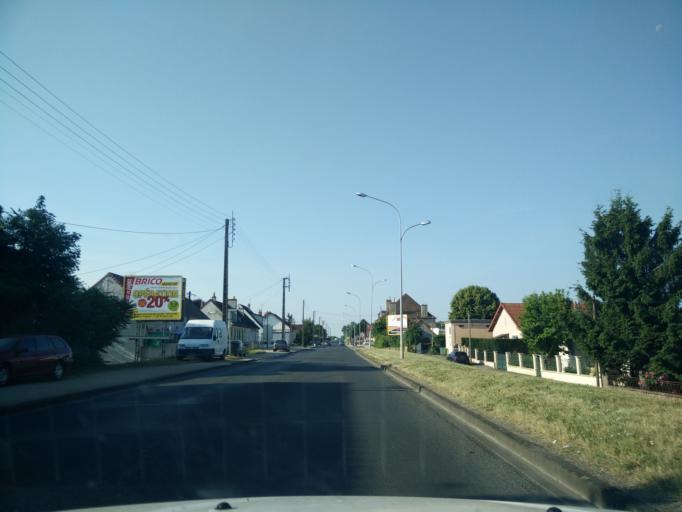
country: FR
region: Auvergne
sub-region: Departement de l'Allier
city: Moulins
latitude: 46.5576
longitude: 3.3212
